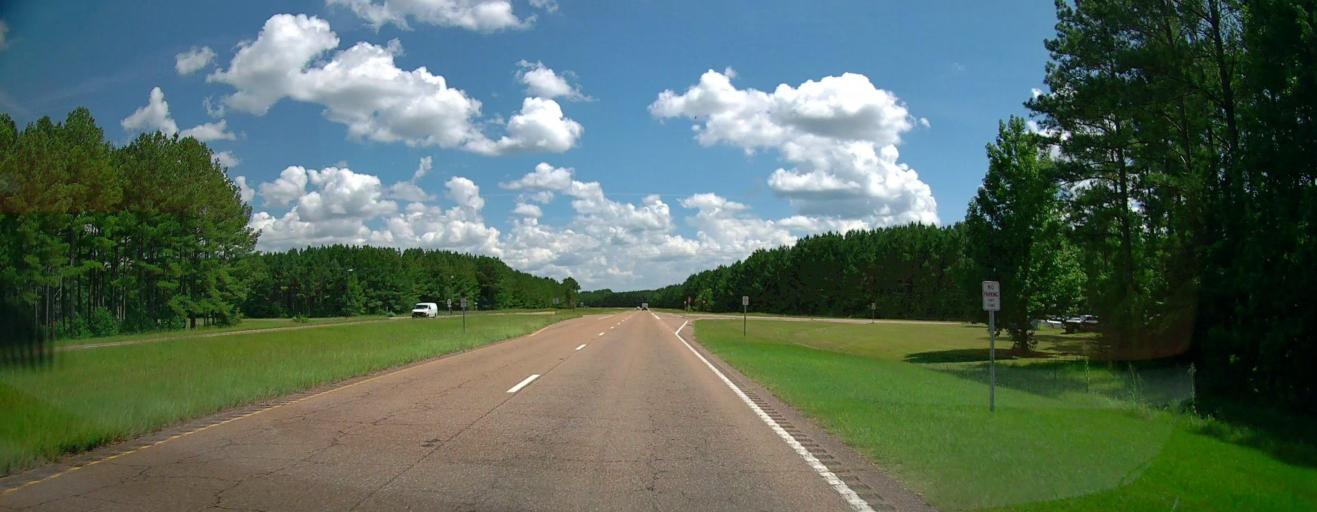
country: US
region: Mississippi
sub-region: Monroe County
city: Aberdeen
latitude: 33.8271
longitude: -88.5857
